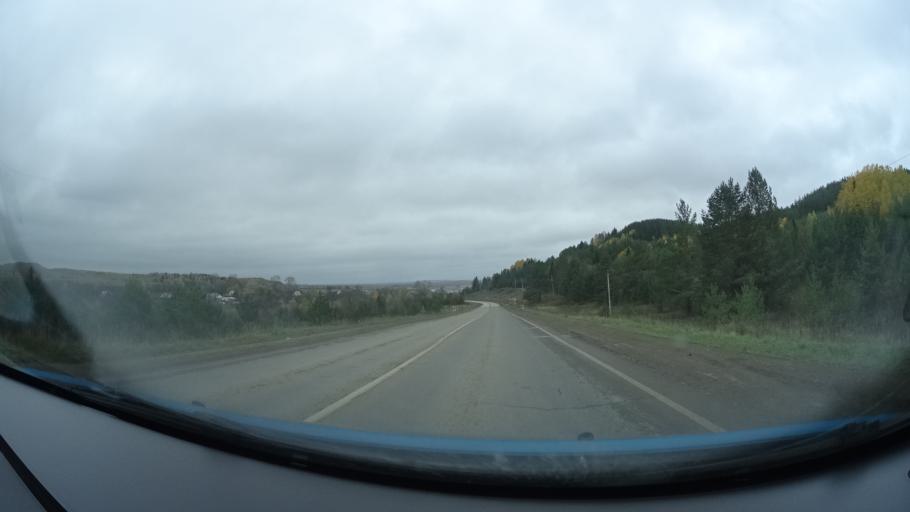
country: RU
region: Perm
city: Osa
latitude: 57.2291
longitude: 55.5908
